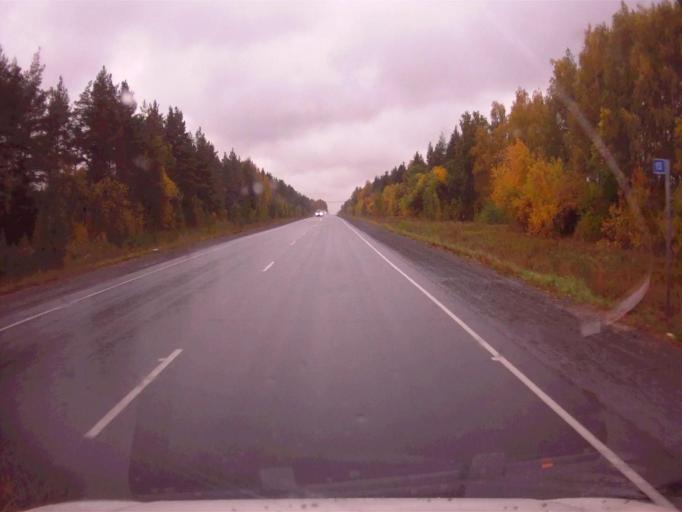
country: RU
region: Chelyabinsk
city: Roshchino
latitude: 55.3781
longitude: 61.1461
